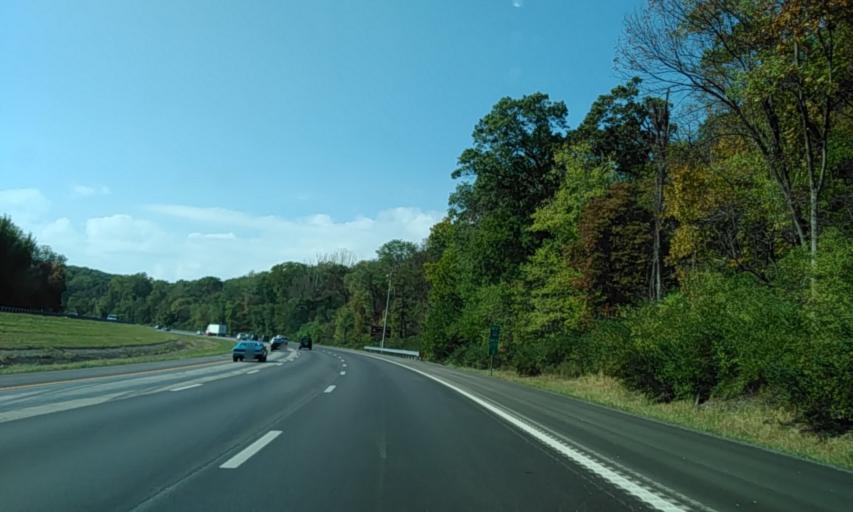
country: US
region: Missouri
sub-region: Saint Louis County
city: Valley Park
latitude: 38.5276
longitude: -90.5409
